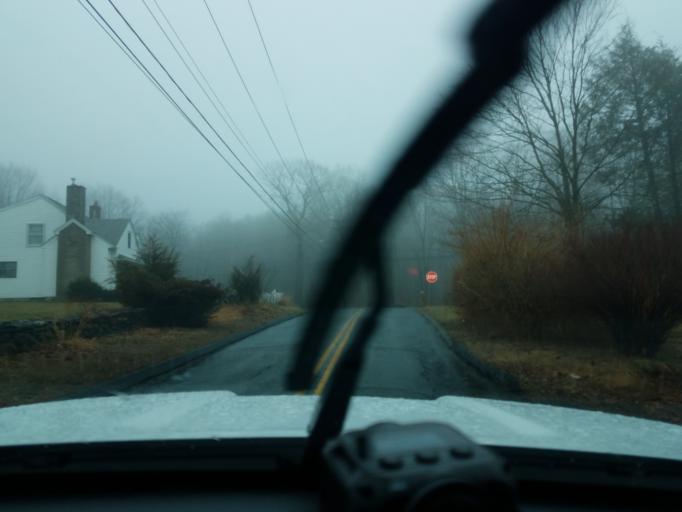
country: US
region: Connecticut
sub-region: New Haven County
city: Naugatuck
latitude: 41.4891
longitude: -73.0288
